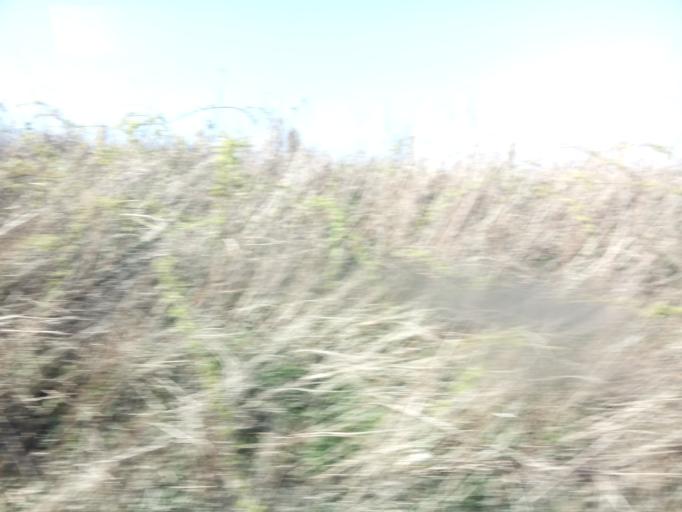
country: GB
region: Scotland
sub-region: East Lothian
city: Dunbar
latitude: 55.9866
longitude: -2.4981
